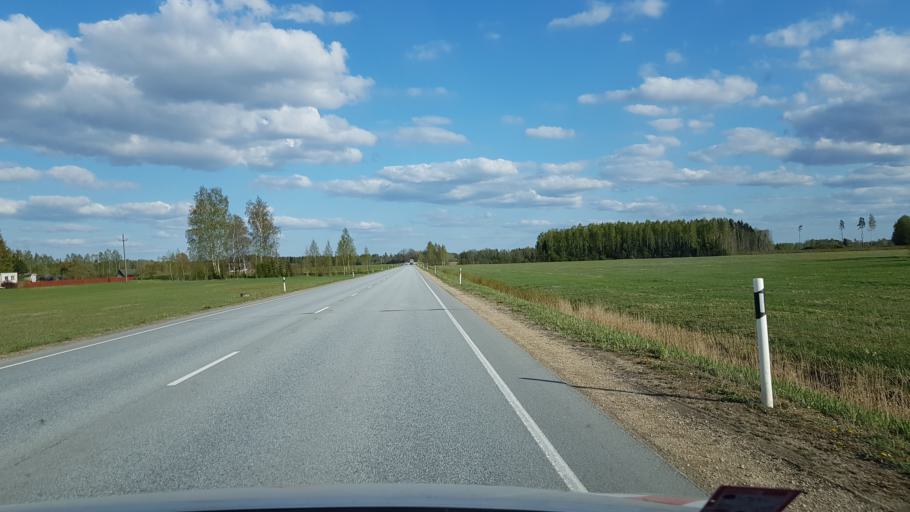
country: EE
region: Vorumaa
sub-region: Voru linn
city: Voru
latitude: 57.9114
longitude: 26.8230
